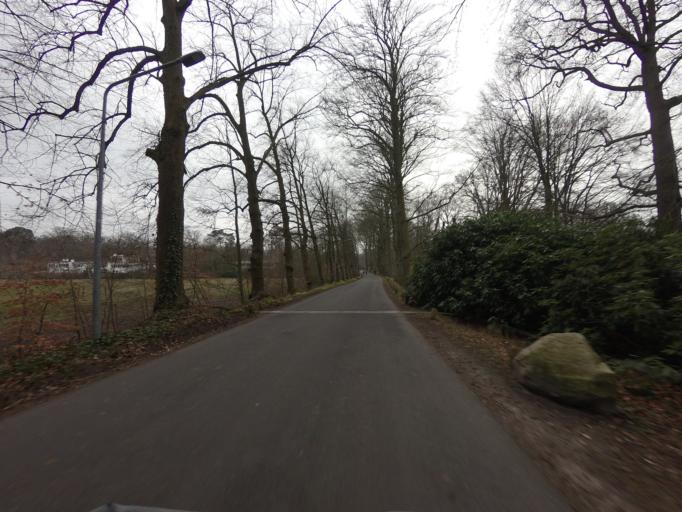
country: NL
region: North Holland
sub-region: Gemeente Wijdemeren
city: Kortenhoef
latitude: 52.2409
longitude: 5.1426
